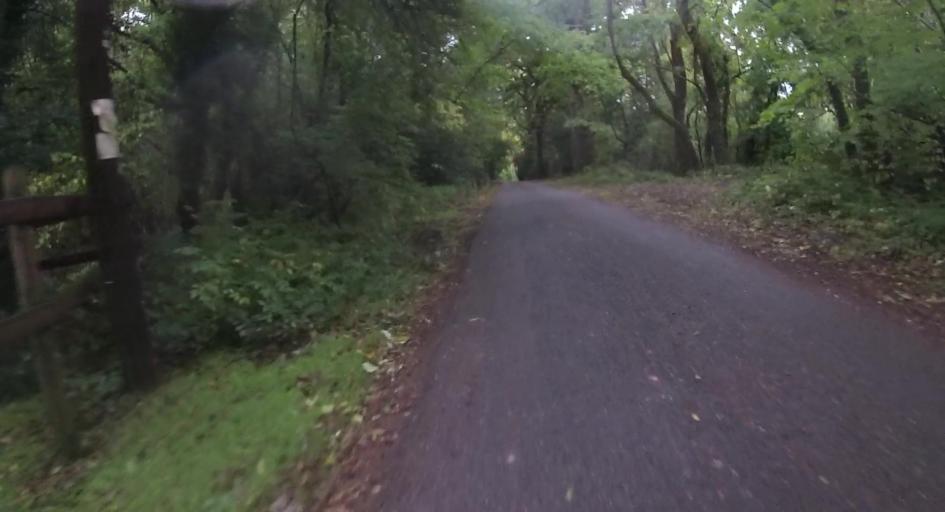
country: GB
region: England
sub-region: Hampshire
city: Tadley
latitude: 51.3546
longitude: -1.1778
